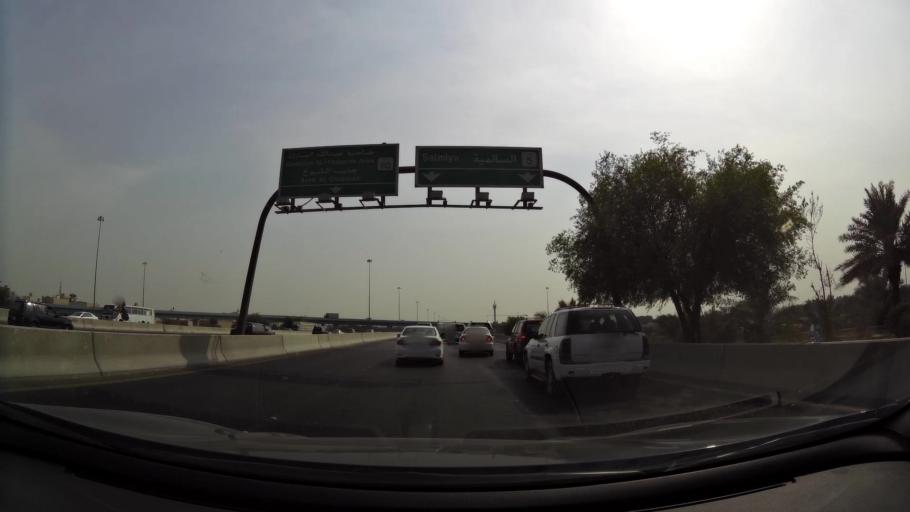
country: KW
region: Al Asimah
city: Ar Rabiyah
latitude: 29.3022
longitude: 47.9450
